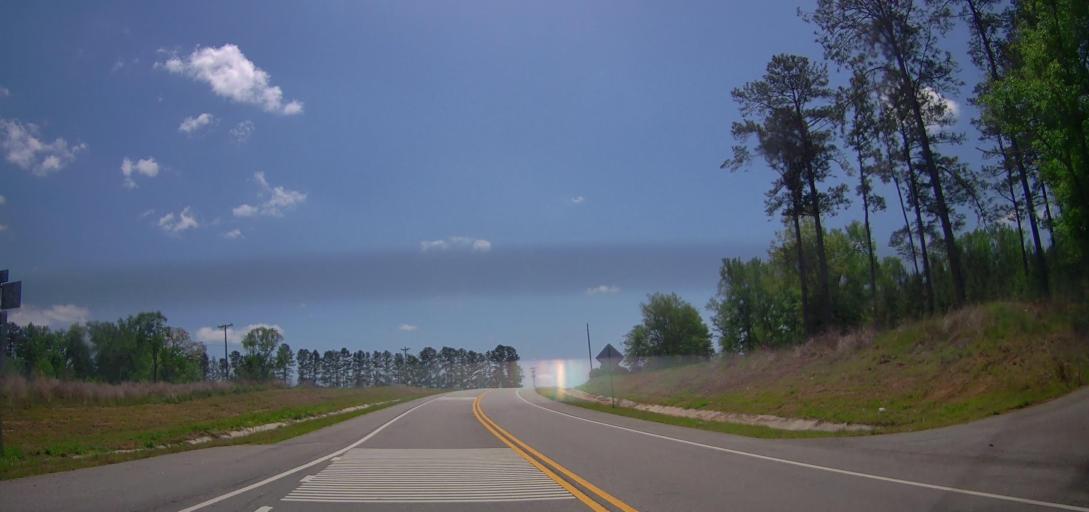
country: US
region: Georgia
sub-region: Jones County
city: Gray
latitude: 33.0167
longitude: -83.5643
